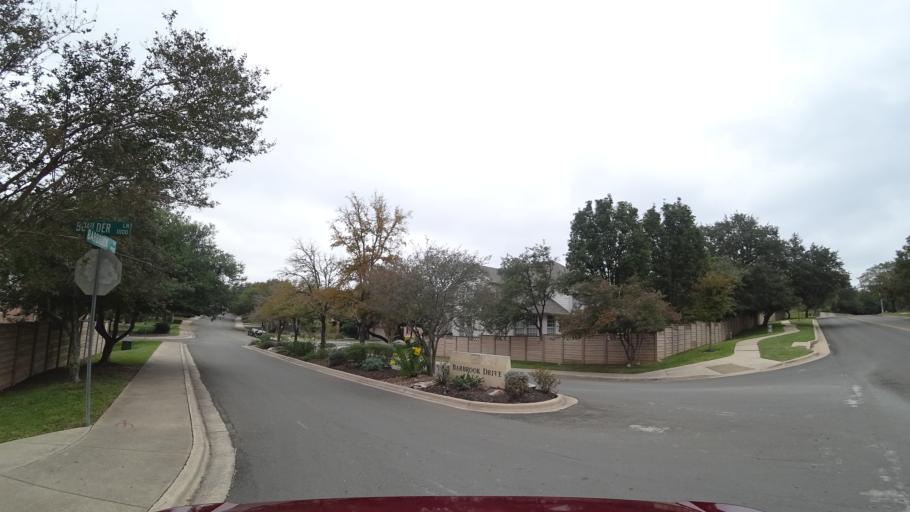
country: US
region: Texas
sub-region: Williamson County
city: Anderson Mill
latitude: 30.4341
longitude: -97.8289
